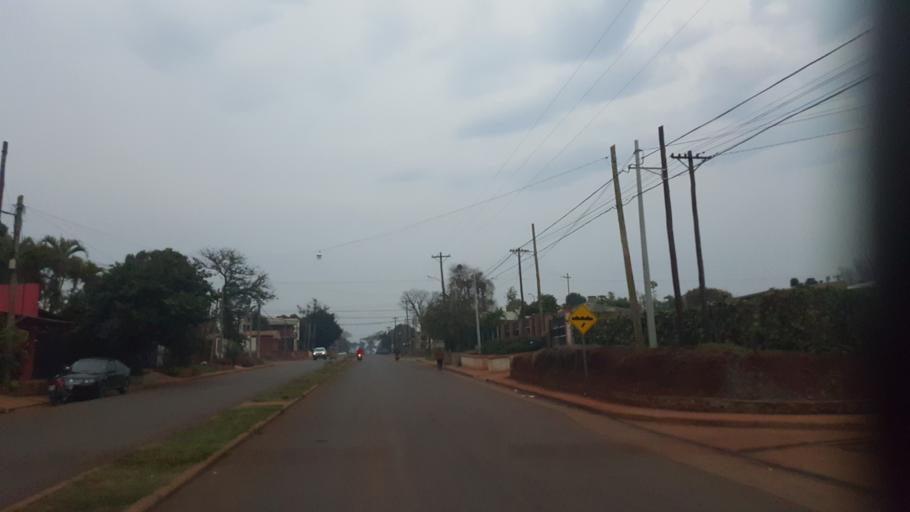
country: AR
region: Misiones
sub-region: Departamento de Capital
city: Posadas
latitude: -27.3967
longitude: -55.9321
